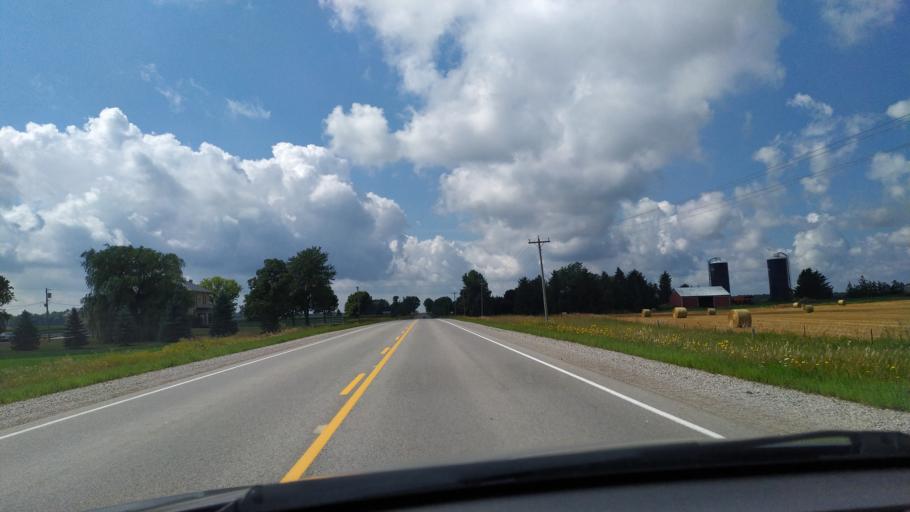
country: CA
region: Ontario
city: Huron East
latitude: 43.4281
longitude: -81.2320
